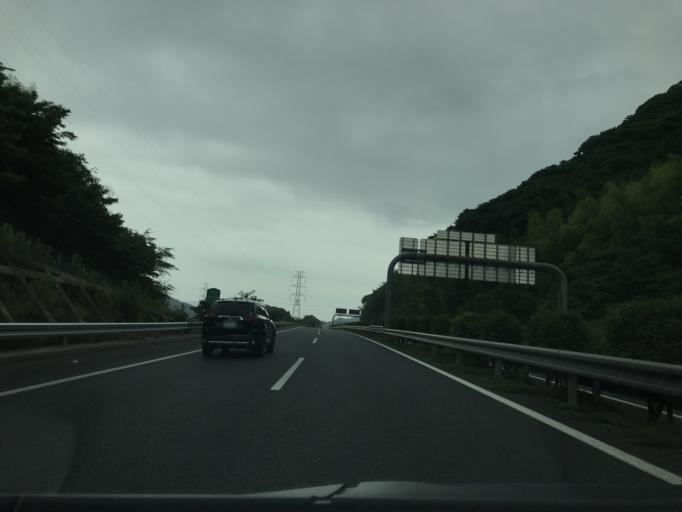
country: JP
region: Fukuoka
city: Kitakyushu
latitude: 33.8148
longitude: 130.8932
